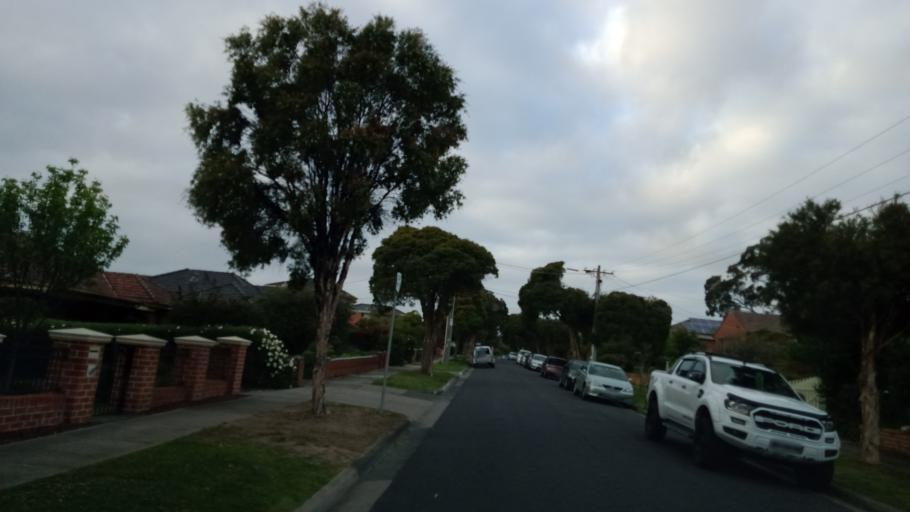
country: AU
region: Victoria
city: Burwood East
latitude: -37.8725
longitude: 145.1459
